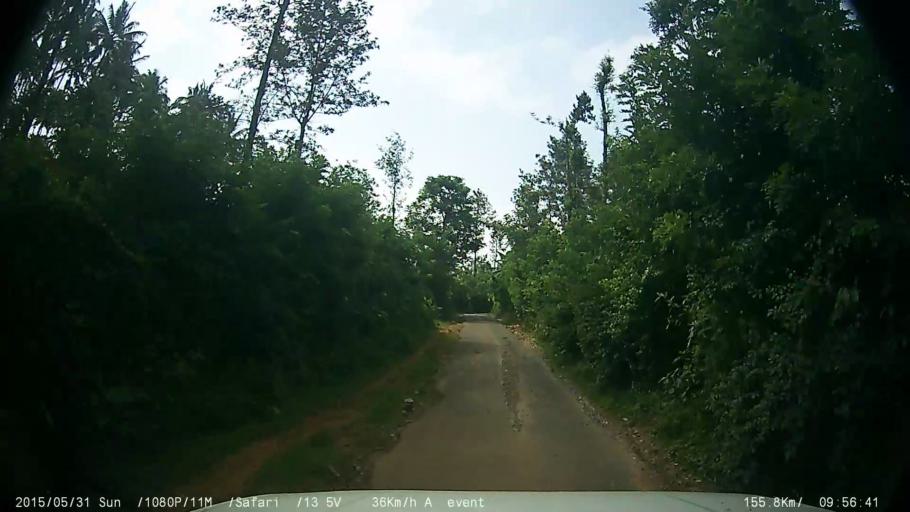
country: IN
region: Kerala
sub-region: Wayanad
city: Kalpetta
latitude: 11.5972
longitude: 76.0568
